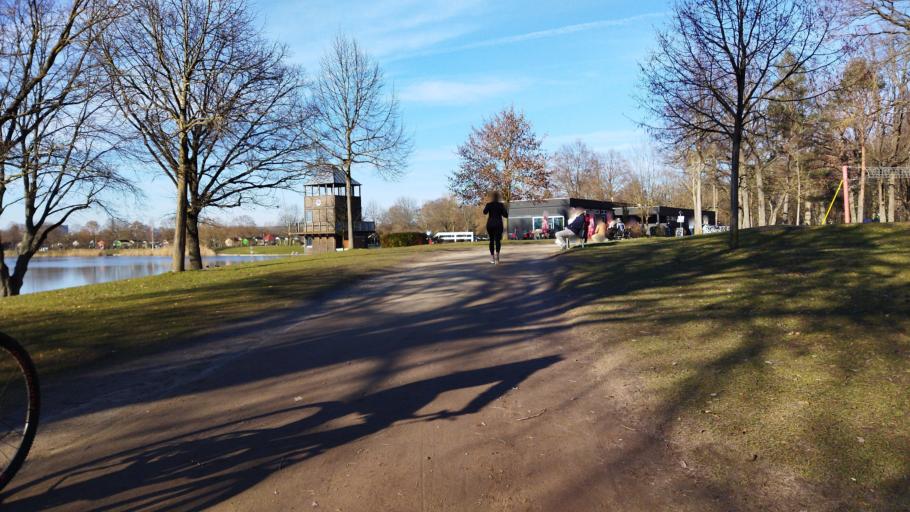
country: DE
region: Bavaria
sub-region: Regierungsbezirk Unterfranken
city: Schwebheim
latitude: 50.0180
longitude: 10.2354
